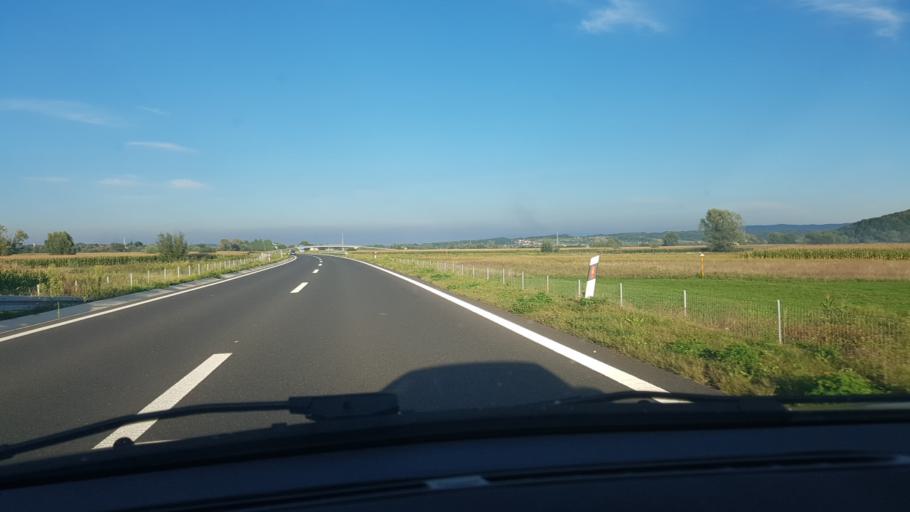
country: HR
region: Krapinsko-Zagorska
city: Selnica
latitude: 46.0395
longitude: 16.0533
